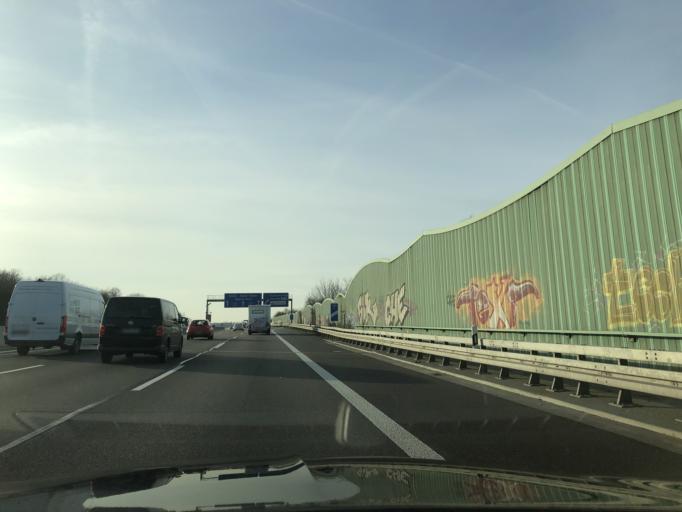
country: DE
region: Baden-Wuerttemberg
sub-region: Karlsruhe Region
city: Ettlingen
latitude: 48.9588
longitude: 8.3907
